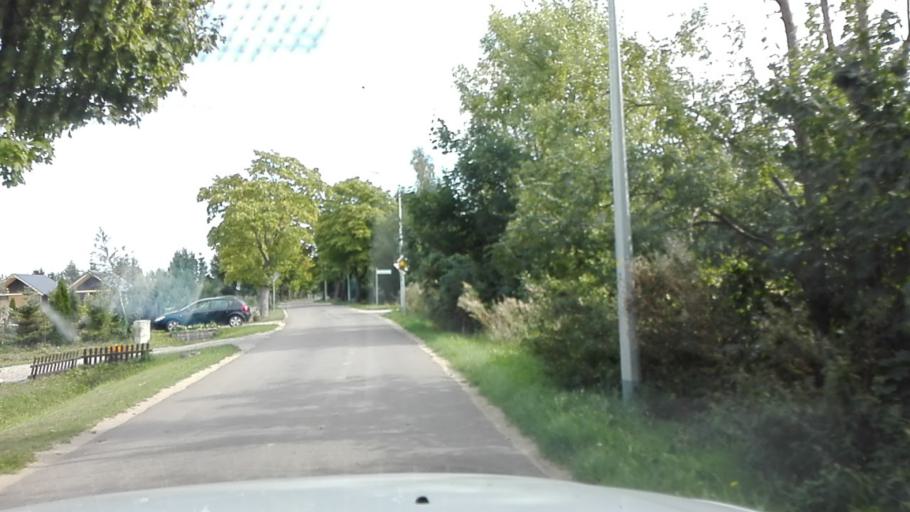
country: PL
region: West Pomeranian Voivodeship
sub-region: Powiat slawienski
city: Slawno
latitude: 54.5310
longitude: 16.5866
